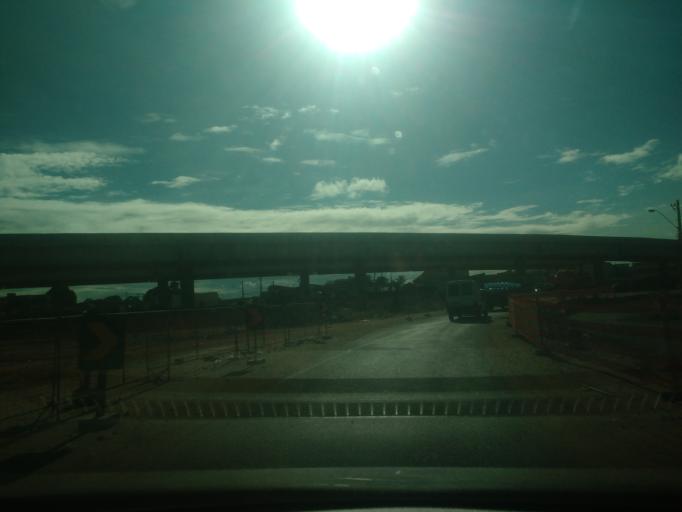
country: BR
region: Alagoas
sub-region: Satuba
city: Satuba
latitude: -9.5655
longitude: -35.7767
